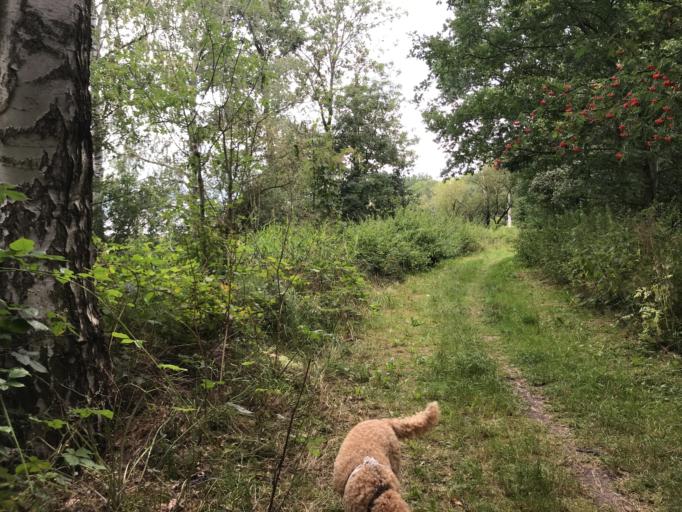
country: CZ
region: Jihocesky
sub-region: Okres Jindrichuv Hradec
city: Lomnice nad Luznici
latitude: 49.0899
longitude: 14.7099
